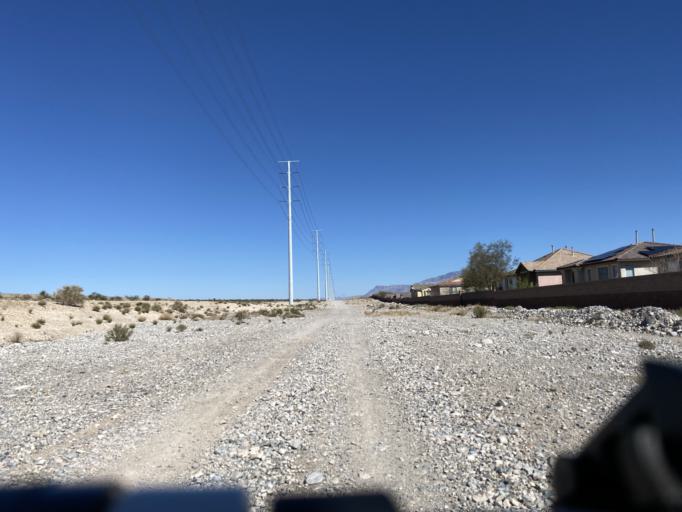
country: US
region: Nevada
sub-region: Clark County
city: Summerlin South
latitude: 36.2886
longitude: -115.3334
